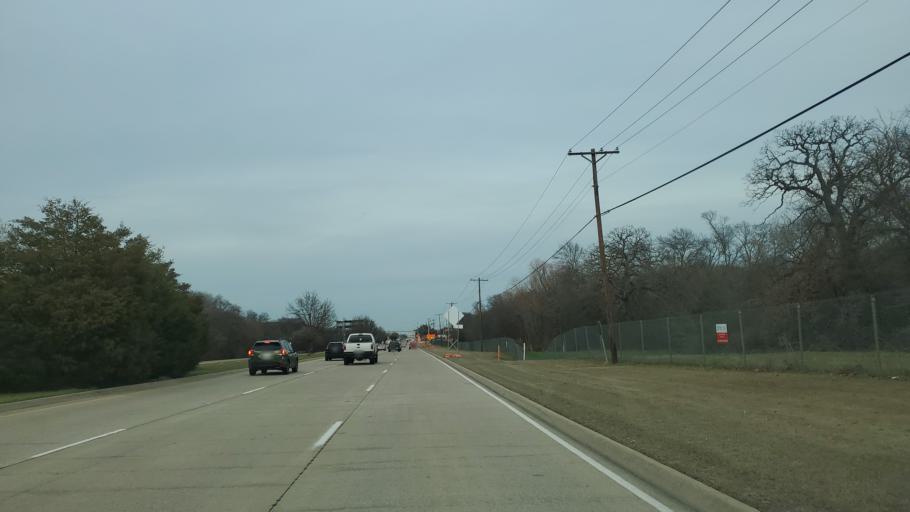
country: US
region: Texas
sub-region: Tarrant County
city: Grapevine
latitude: 32.9525
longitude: -97.0510
